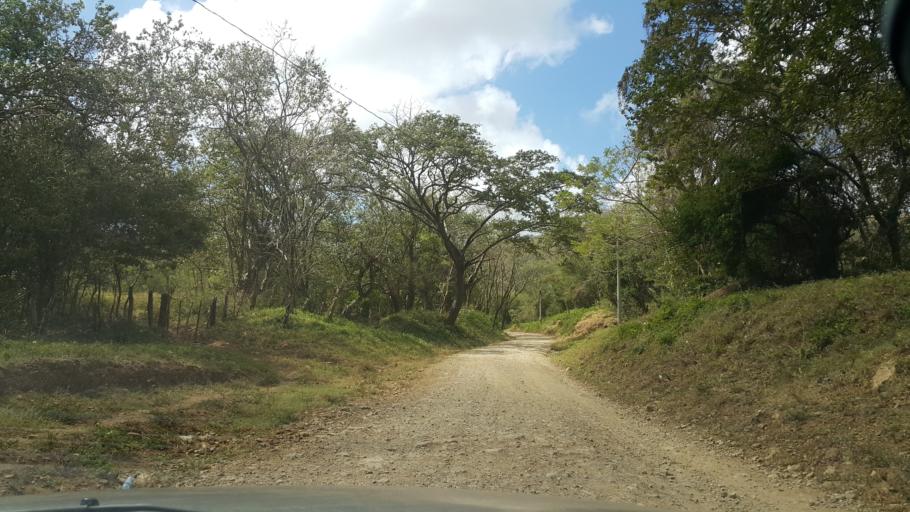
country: NI
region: Rivas
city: San Juan del Sur
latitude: 11.3049
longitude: -85.8573
